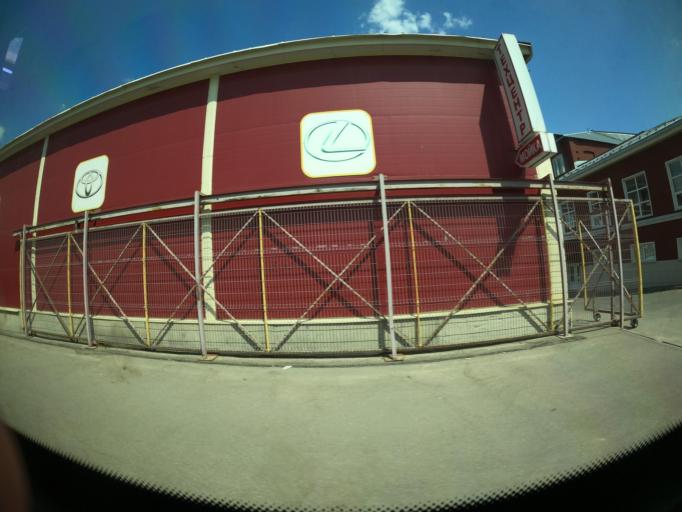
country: RU
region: Moskovskaya
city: Serpukhov
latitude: 54.9218
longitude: 37.3817
